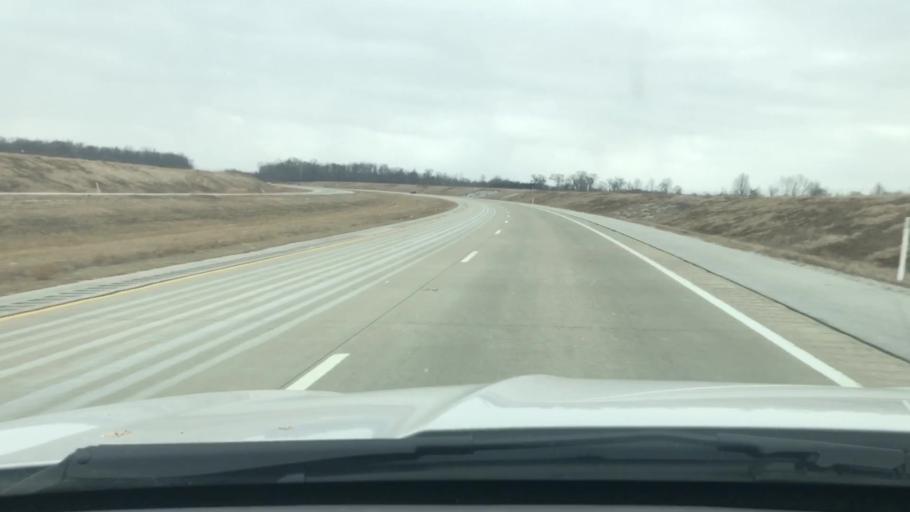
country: US
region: Indiana
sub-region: Carroll County
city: Delphi
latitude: 40.5255
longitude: -86.7125
